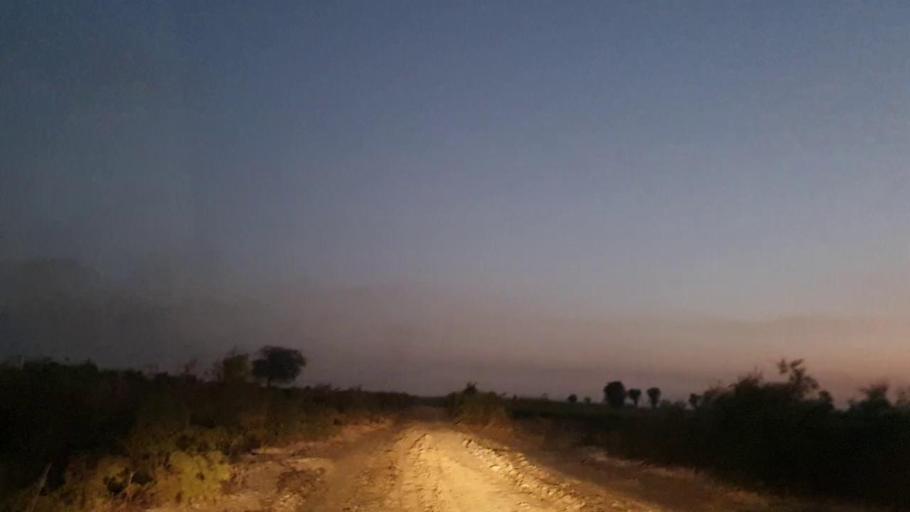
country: PK
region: Sindh
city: Nawabshah
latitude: 26.3294
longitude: 68.3757
